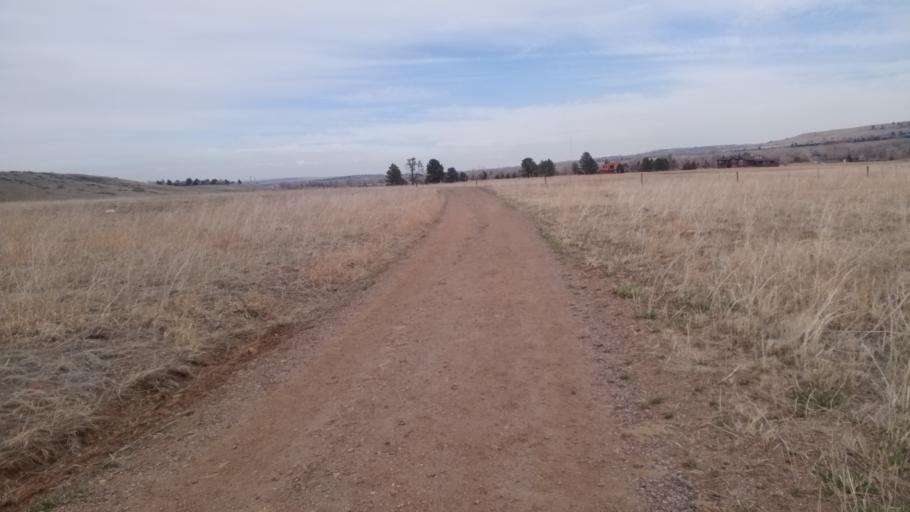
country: US
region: Colorado
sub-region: Boulder County
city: Boulder
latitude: 39.9591
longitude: -105.2468
